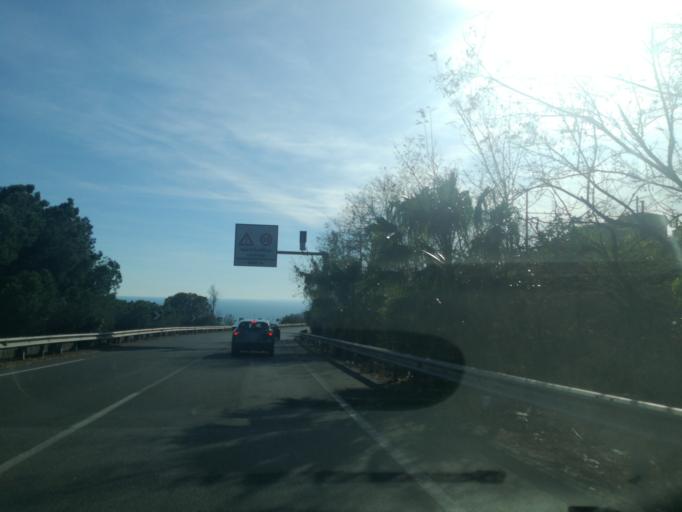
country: IT
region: Sicily
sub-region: Catania
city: Acireale
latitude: 37.6143
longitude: 15.1710
